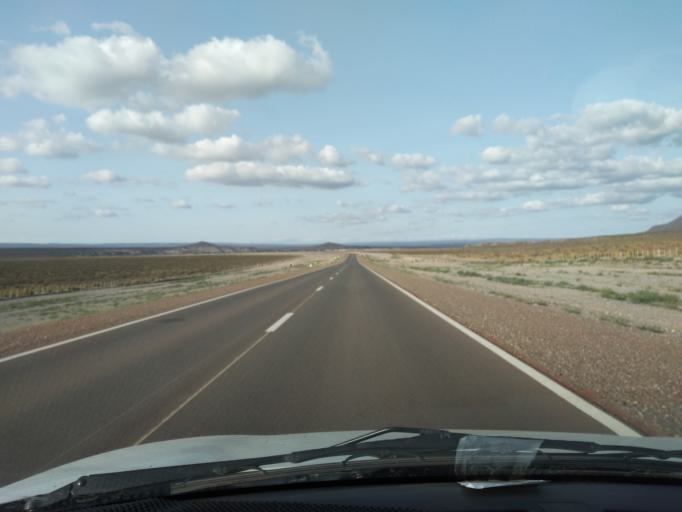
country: AR
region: Mendoza
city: San Rafael
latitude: -34.6552
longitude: -69.1591
